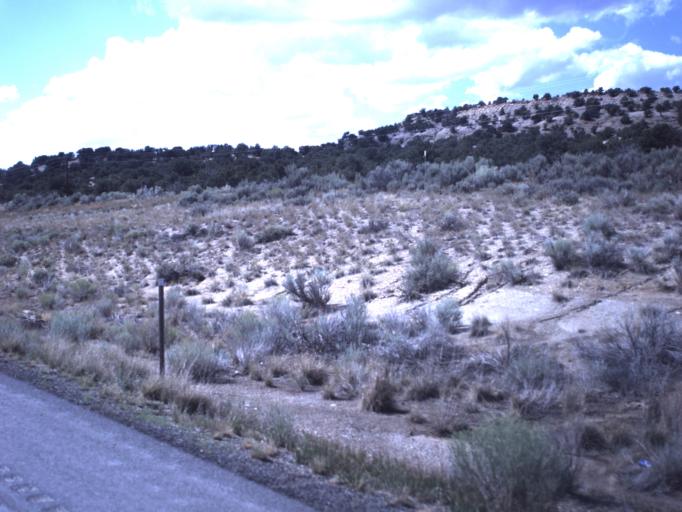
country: US
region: Utah
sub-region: Duchesne County
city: Duchesne
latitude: 40.1722
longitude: -110.5819
